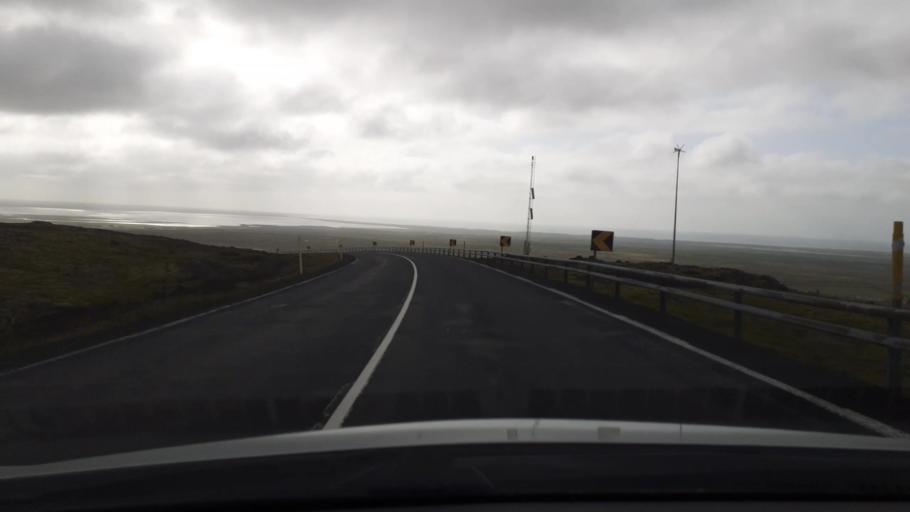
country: IS
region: South
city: THorlakshoefn
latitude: 63.9316
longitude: -21.3930
